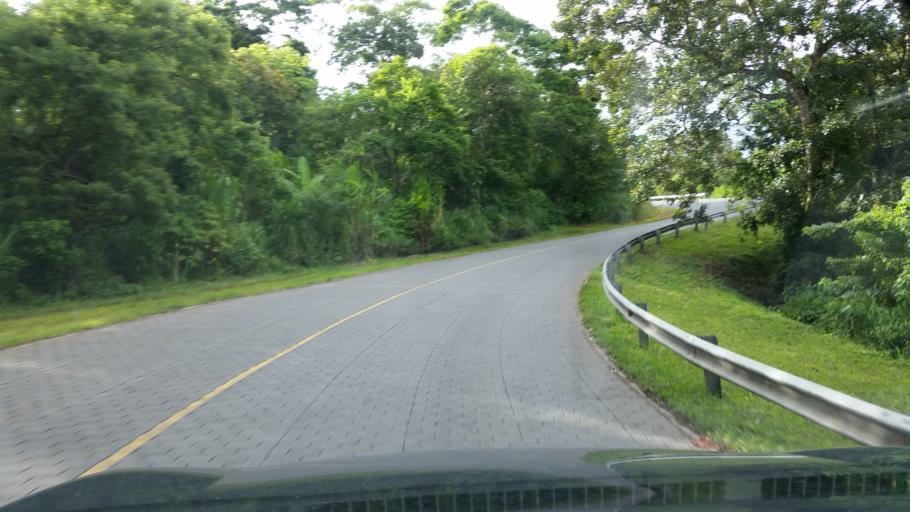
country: NI
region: Matagalpa
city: San Ramon
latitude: 13.1723
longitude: -85.7281
